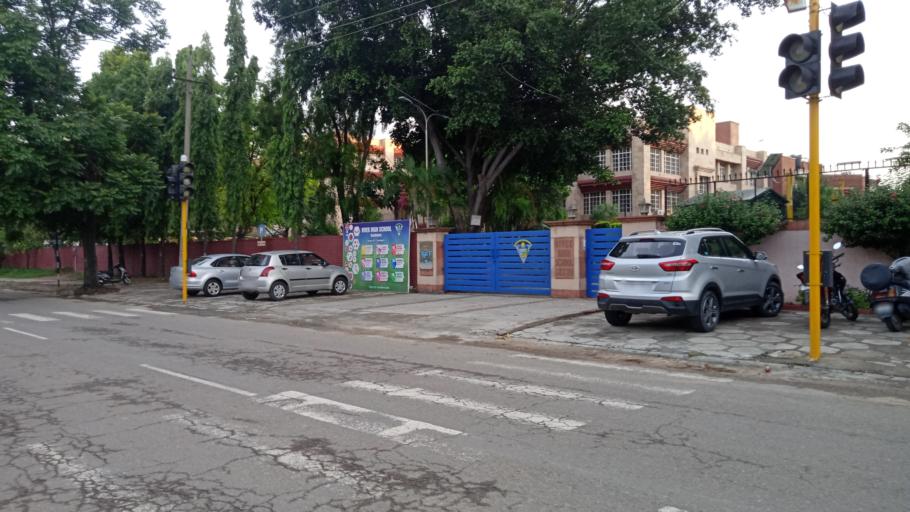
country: IN
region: Chandigarh
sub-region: Chandigarh
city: Chandigarh
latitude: 30.7465
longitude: 76.7492
